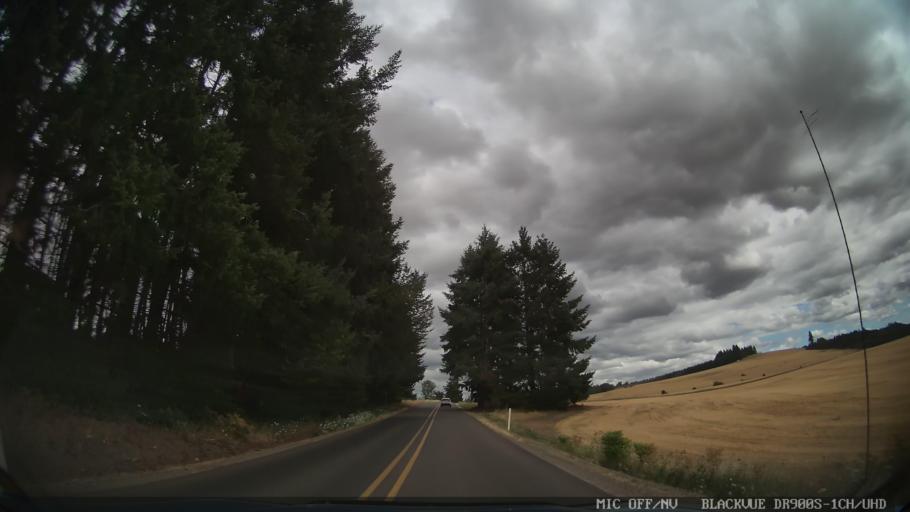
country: US
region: Oregon
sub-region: Marion County
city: Sublimity
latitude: 44.8670
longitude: -122.7446
